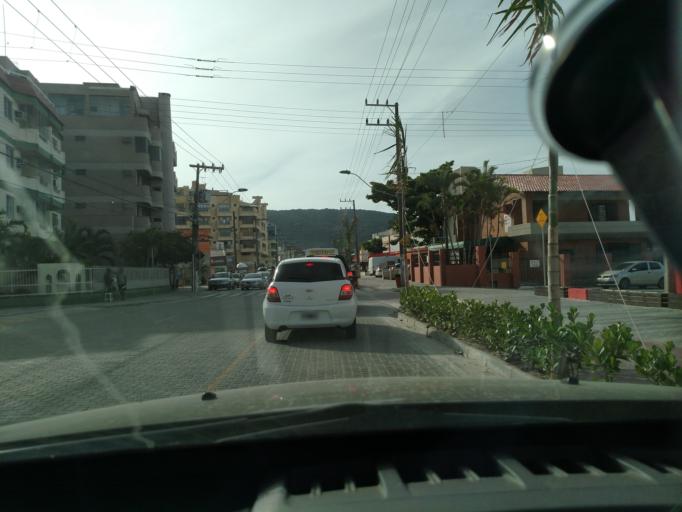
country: BR
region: Santa Catarina
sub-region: Porto Belo
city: Porto Belo
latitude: -27.1434
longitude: -48.5056
